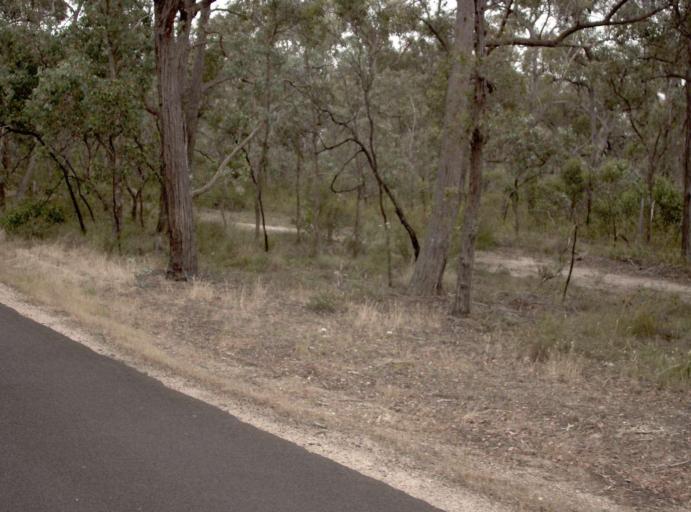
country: AU
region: Victoria
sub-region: Wellington
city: Heyfield
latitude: -37.9530
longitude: 146.7692
